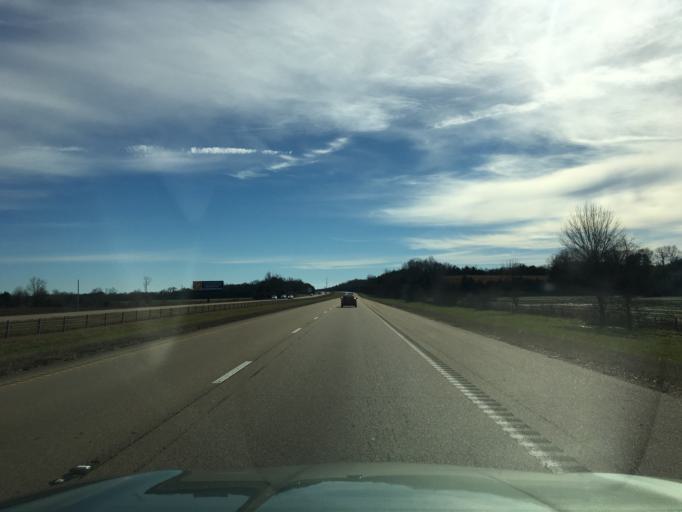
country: US
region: Mississippi
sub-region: Lee County
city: Tupelo
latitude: 34.3430
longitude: -88.8312
